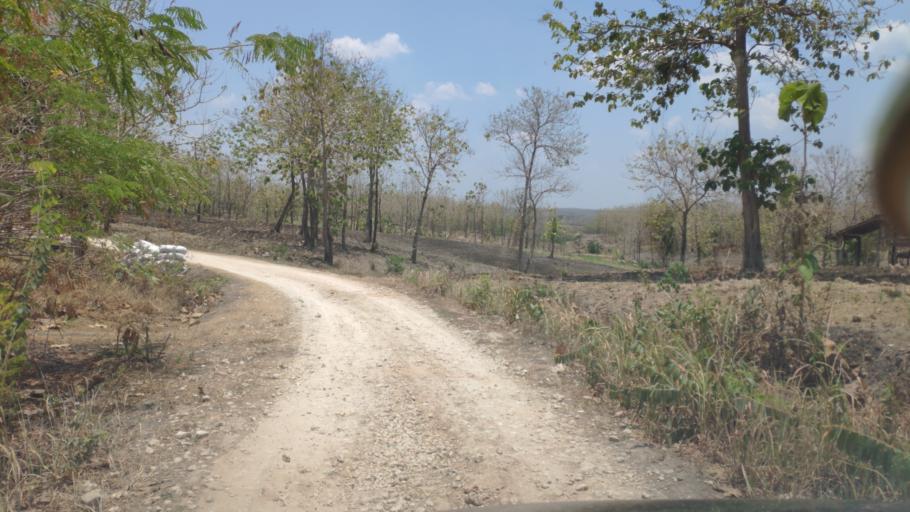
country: ID
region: West Java
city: Ngawi
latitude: -7.3294
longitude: 111.3619
